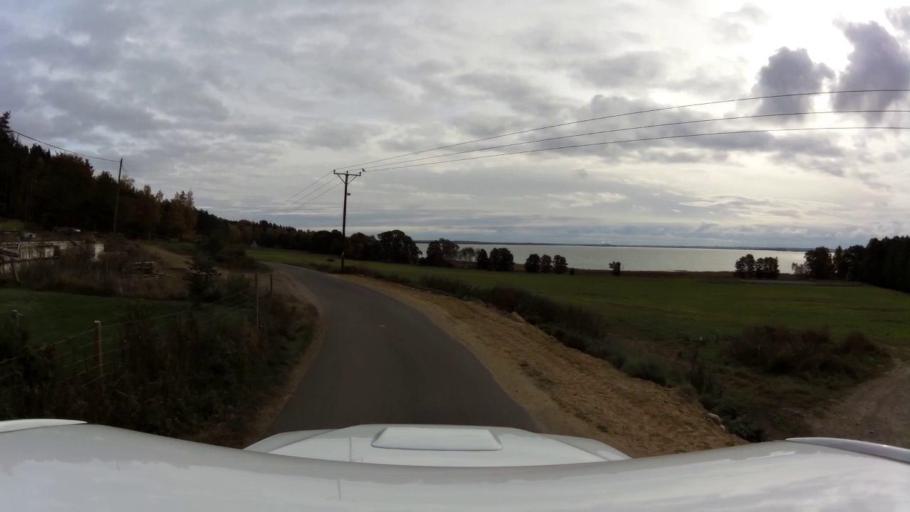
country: SE
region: OEstergoetland
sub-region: Linkopings Kommun
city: Berg
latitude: 58.5116
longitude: 15.5534
